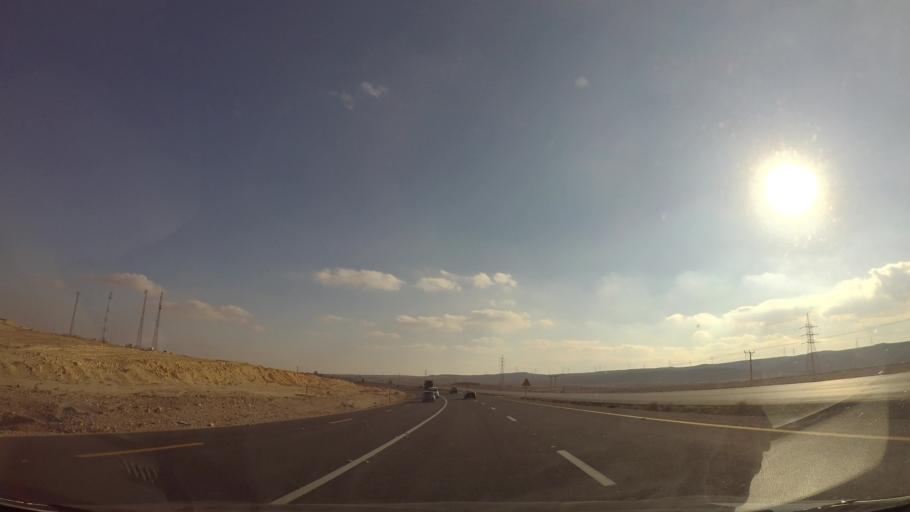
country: JO
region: Karak
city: Karak City
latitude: 31.1141
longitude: 36.0073
